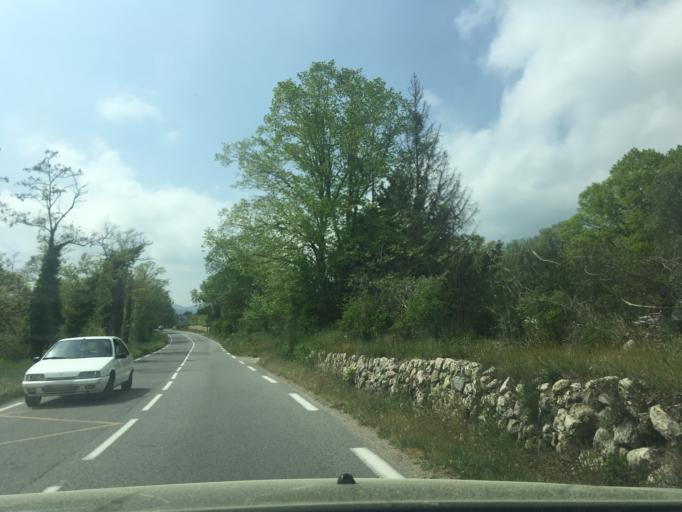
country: FR
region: Provence-Alpes-Cote d'Azur
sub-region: Departement du Var
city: Fayence
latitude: 43.6174
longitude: 6.7131
